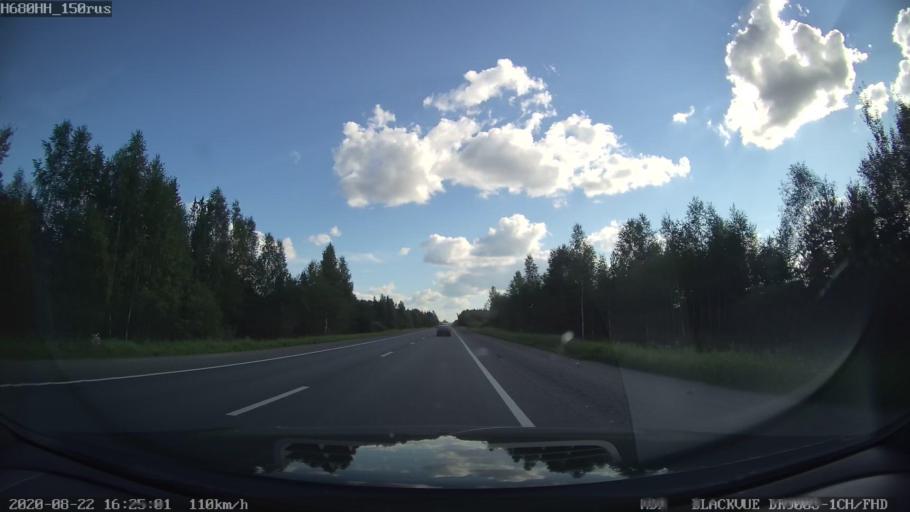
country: RU
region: Tverskaya
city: Rameshki
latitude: 57.3278
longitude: 36.0922
